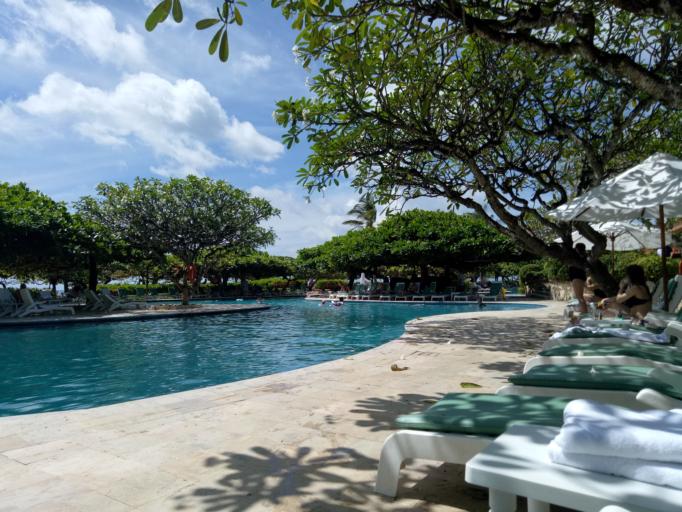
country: ID
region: Bali
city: Bualu
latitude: -8.8036
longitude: 115.2346
